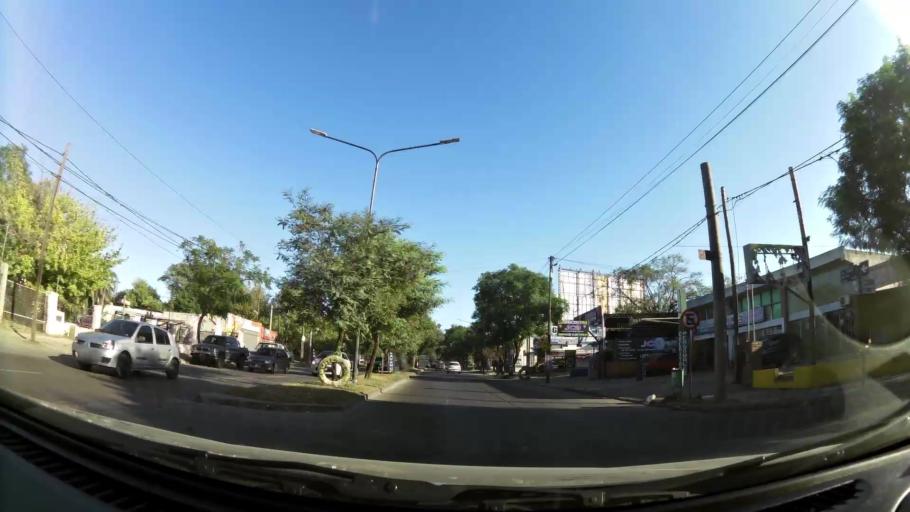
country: AR
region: Cordoba
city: Villa Allende
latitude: -31.3434
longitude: -64.2522
